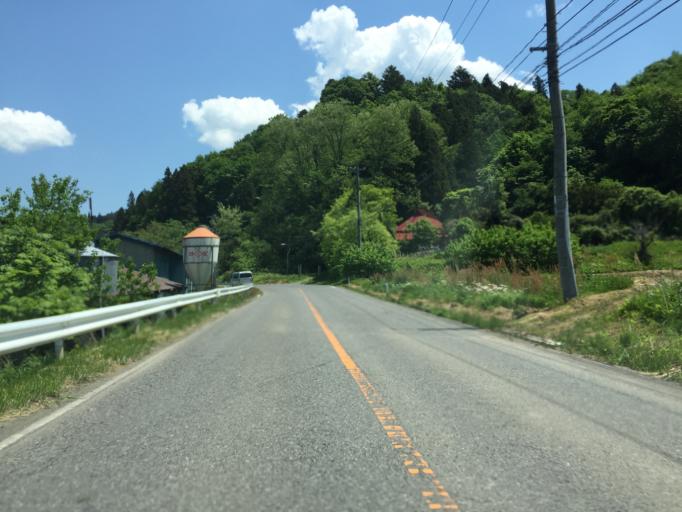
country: JP
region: Fukushima
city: Funehikimachi-funehiki
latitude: 37.4962
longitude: 140.5879
